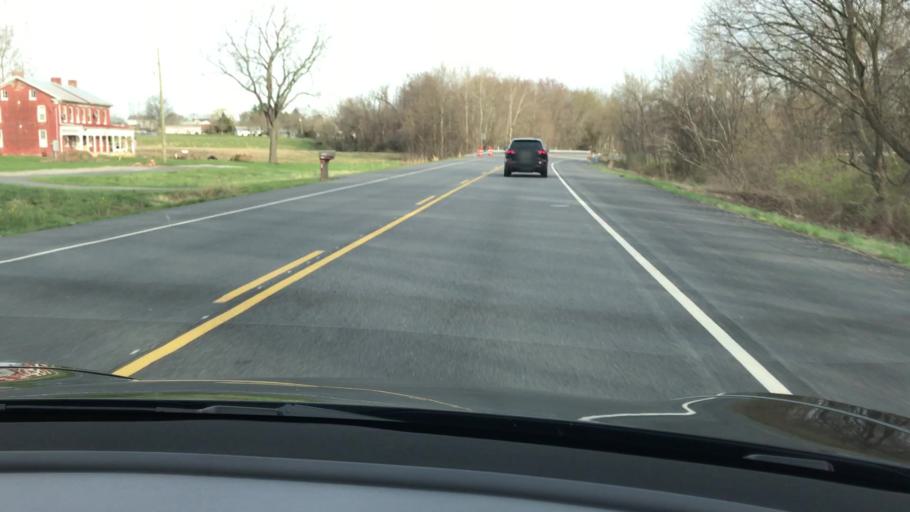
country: US
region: Pennsylvania
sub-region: York County
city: Valley Green
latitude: 40.1391
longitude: -76.8680
